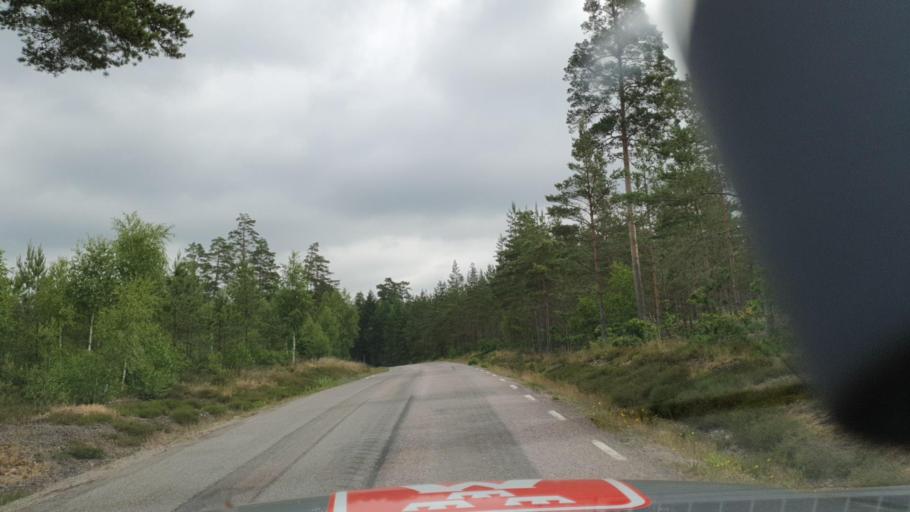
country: SE
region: Kalmar
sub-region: Torsas Kommun
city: Torsas
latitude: 56.4895
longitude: 16.0988
